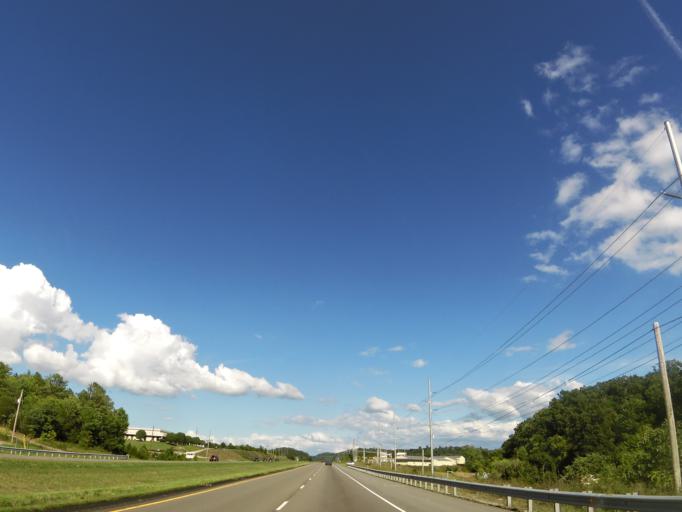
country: US
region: Tennessee
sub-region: Greene County
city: Mosheim
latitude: 36.1730
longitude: -82.9121
